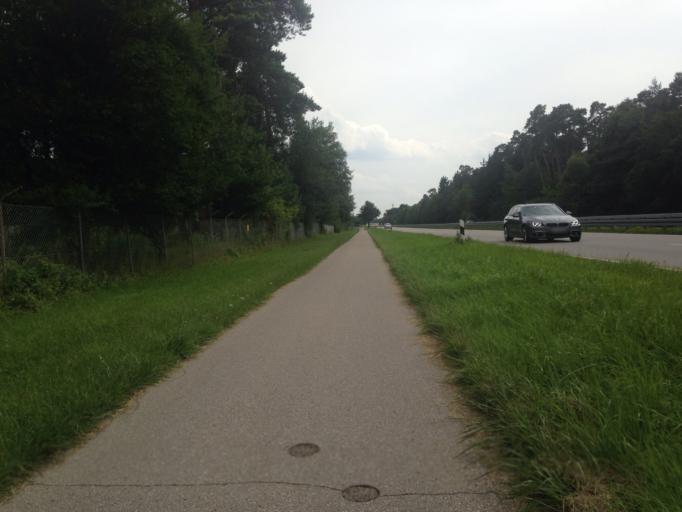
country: DE
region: Bavaria
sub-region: Upper Bavaria
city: Oberschleissheim
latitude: 48.2398
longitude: 11.6006
